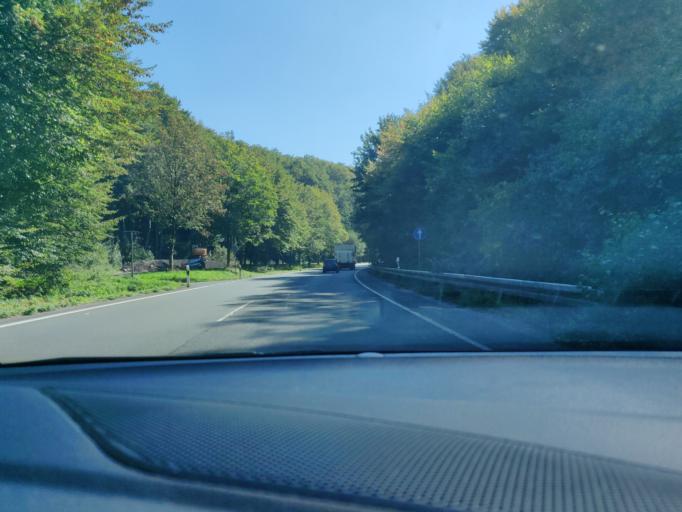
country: DE
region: North Rhine-Westphalia
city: Sprockhovel
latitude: 51.3585
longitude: 7.2022
